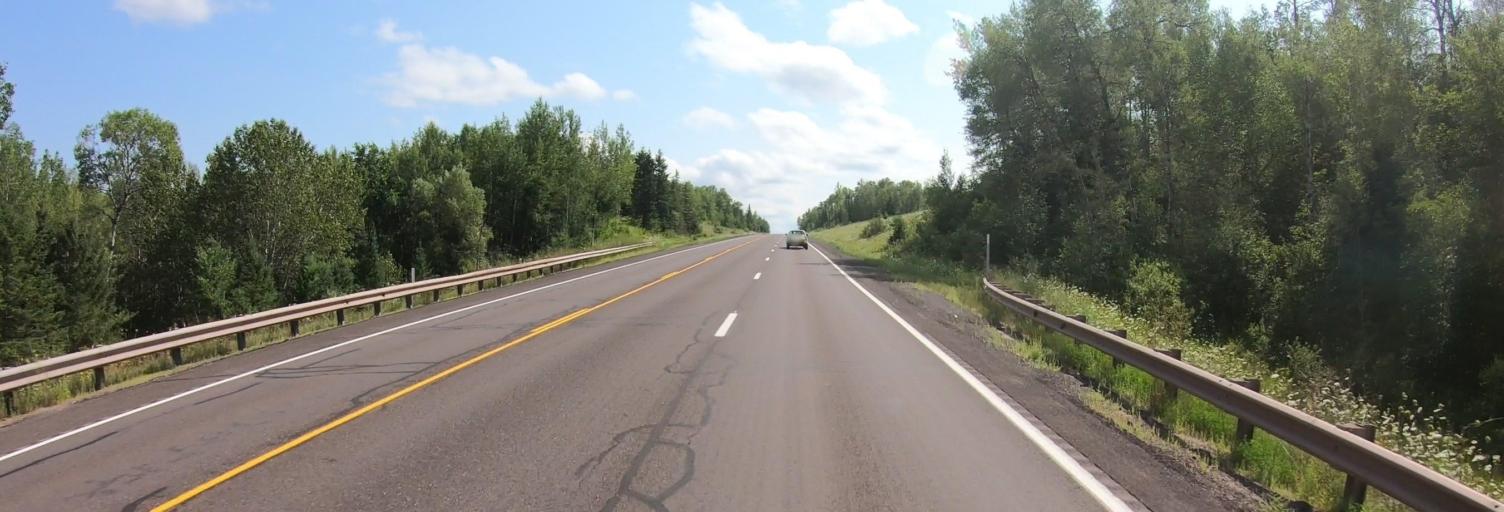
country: US
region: Michigan
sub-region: Ontonagon County
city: Ontonagon
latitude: 46.6767
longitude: -89.1671
